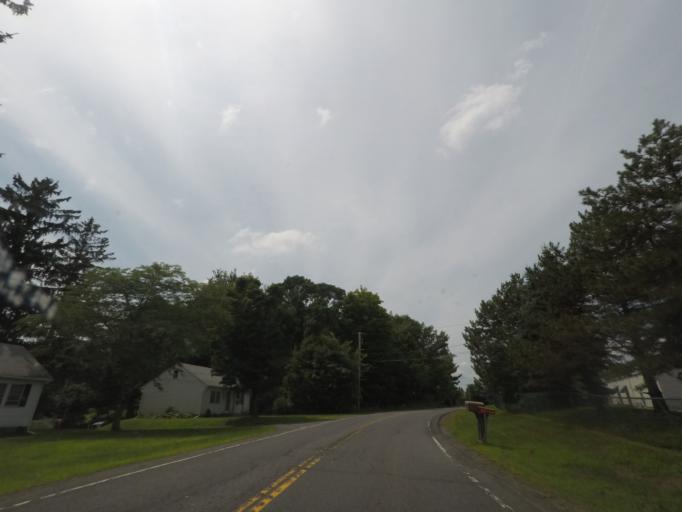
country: US
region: New York
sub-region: Rensselaer County
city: Wynantskill
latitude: 42.7444
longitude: -73.6398
